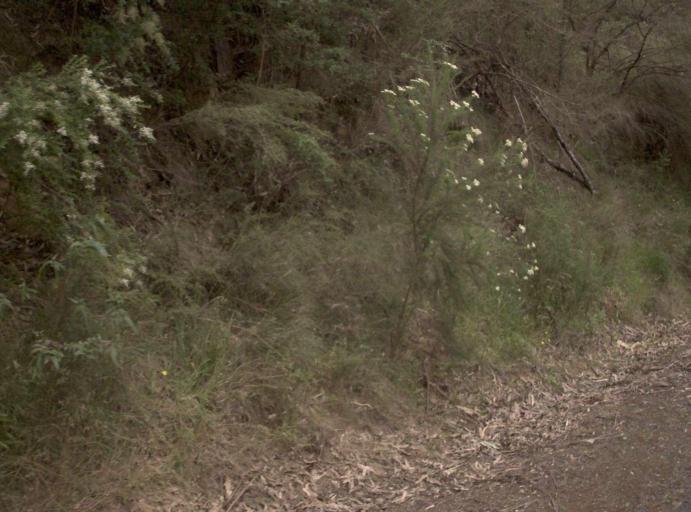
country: AU
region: New South Wales
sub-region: Bombala
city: Bombala
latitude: -37.4255
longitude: 149.2000
